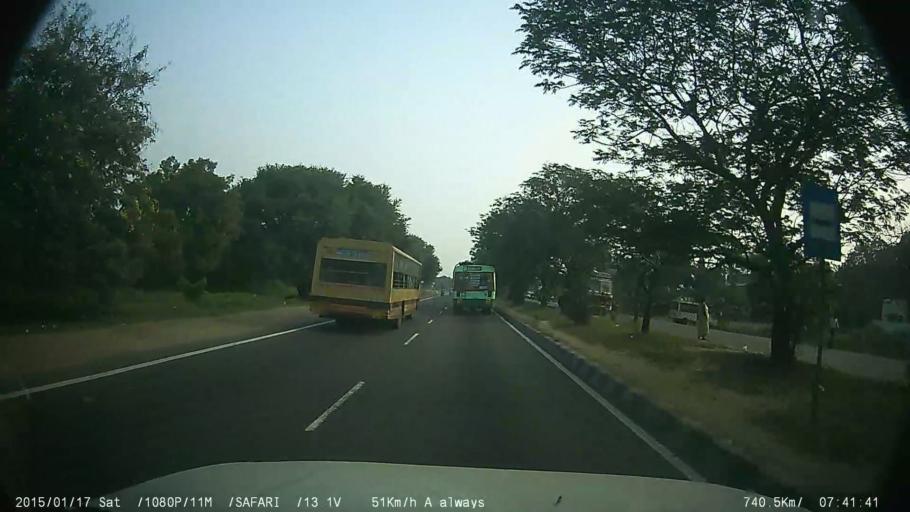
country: IN
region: Tamil Nadu
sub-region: Kancheepuram
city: Singapperumalkovil
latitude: 12.7976
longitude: 80.0217
